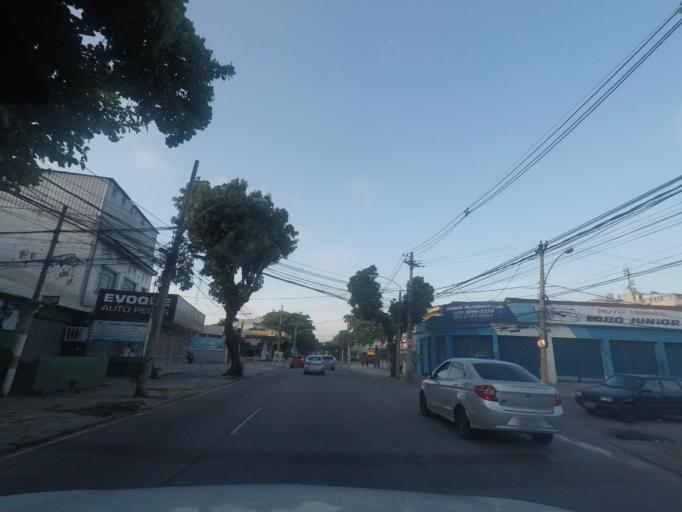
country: BR
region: Rio de Janeiro
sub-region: Duque De Caxias
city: Duque de Caxias
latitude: -22.8298
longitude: -43.2773
